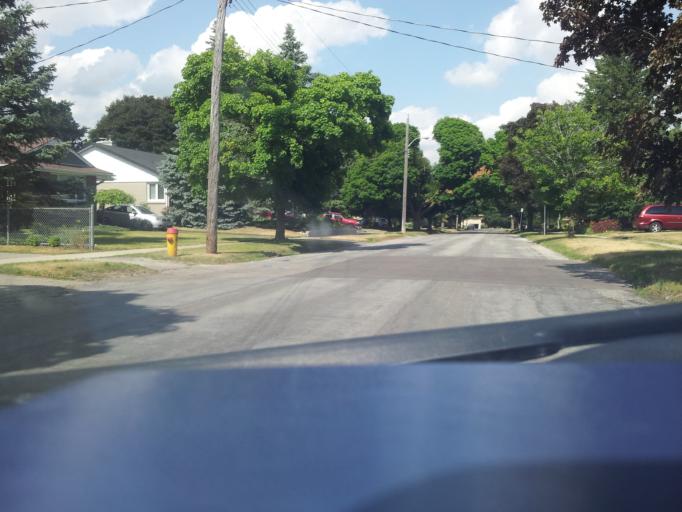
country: CA
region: Ontario
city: Waterloo
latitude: 43.4480
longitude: -80.5215
